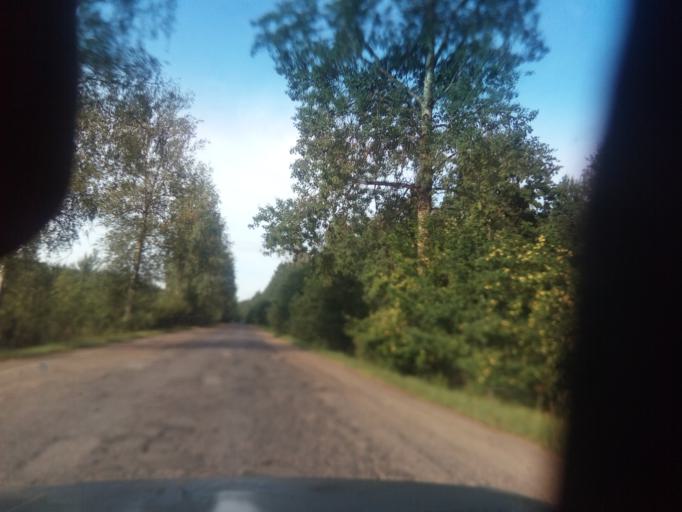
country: BY
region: Vitebsk
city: Dzisna
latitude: 55.6388
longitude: 28.3115
